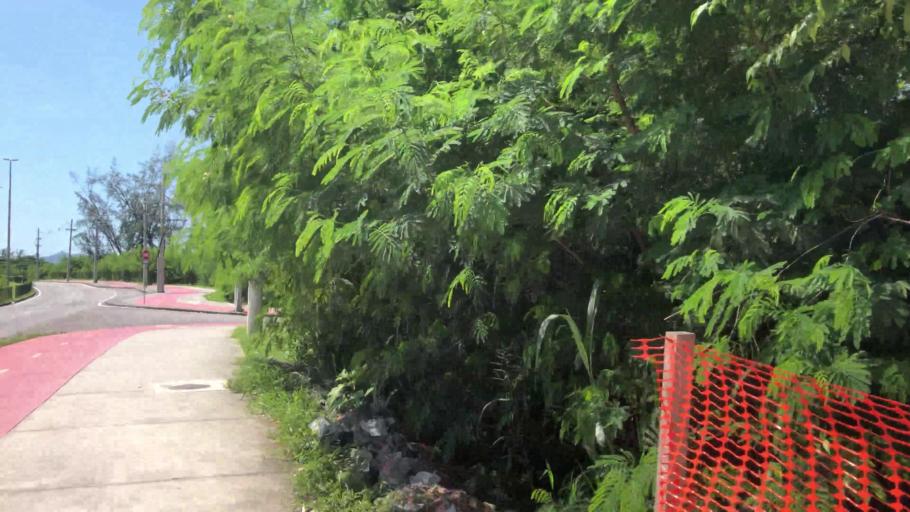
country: BR
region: Rio de Janeiro
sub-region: Nilopolis
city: Nilopolis
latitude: -22.9735
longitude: -43.3982
